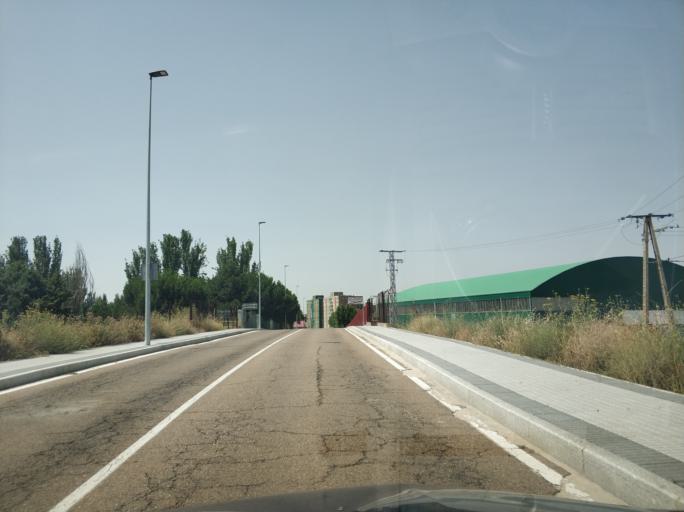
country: ES
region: Castille and Leon
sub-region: Provincia de Salamanca
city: Carbajosa de la Sagrada
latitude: 40.9453
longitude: -5.6596
